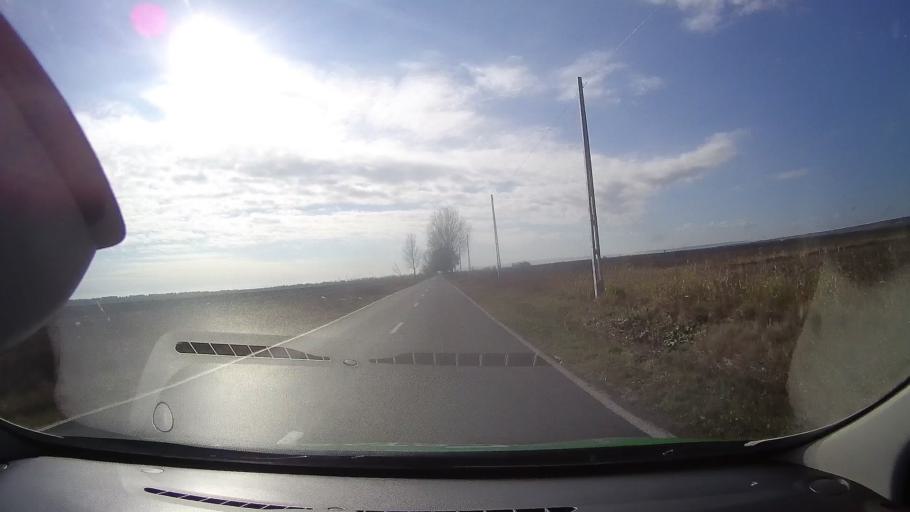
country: RO
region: Tulcea
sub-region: Comuna Valea Nucarilor
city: Agighiol
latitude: 44.9939
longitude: 28.8862
